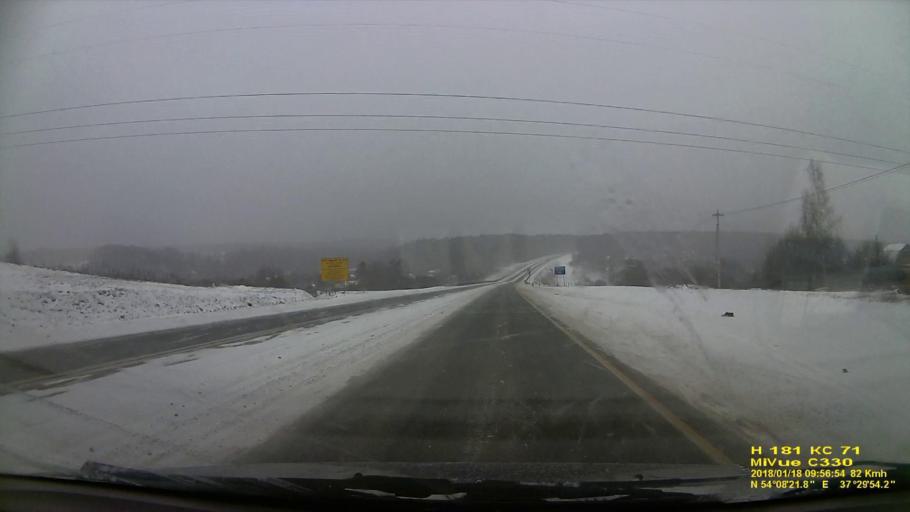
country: RU
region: Tula
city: Kosaya Gora
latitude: 54.1393
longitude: 37.4984
